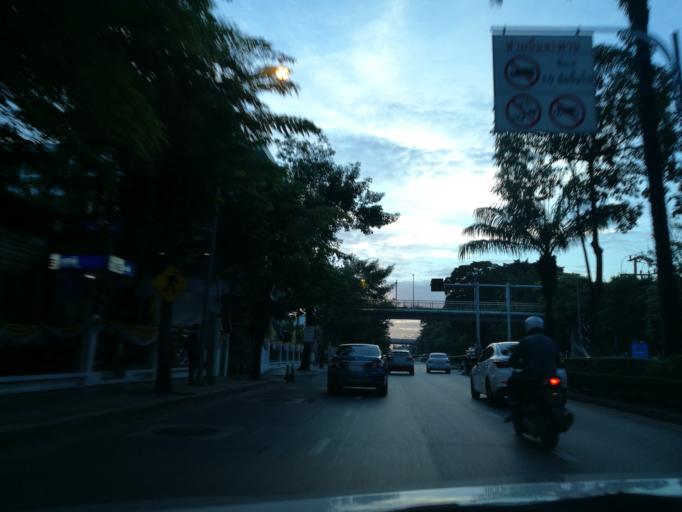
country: TH
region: Bangkok
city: Ratchathewi
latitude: 13.7673
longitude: 100.5335
